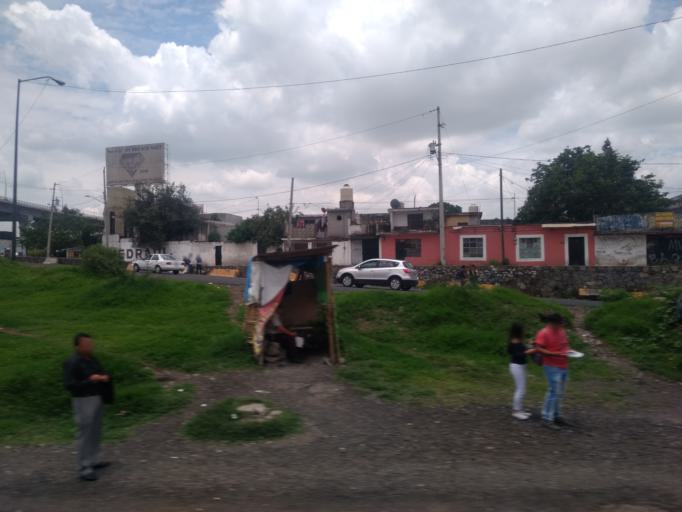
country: MX
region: Puebla
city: Puebla
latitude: 19.0859
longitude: -98.2051
